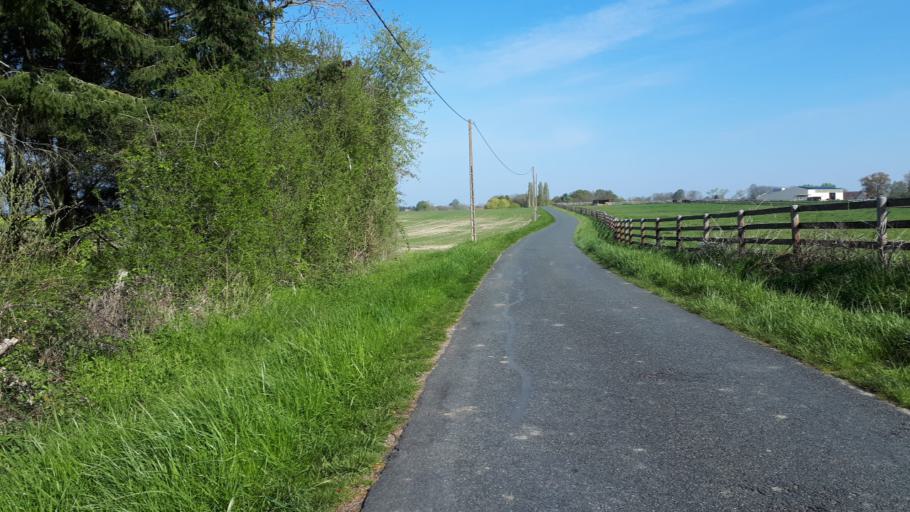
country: FR
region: Centre
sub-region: Departement du Loir-et-Cher
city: Saint-Romain-sur-Cher
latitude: 47.3724
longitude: 1.3979
